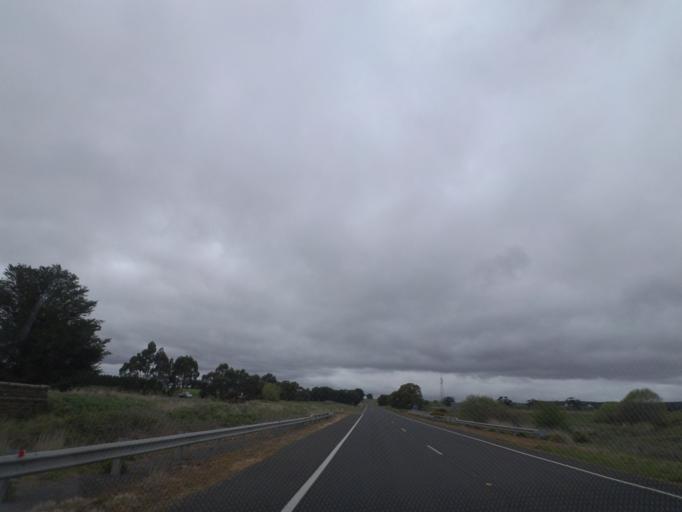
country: AU
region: Victoria
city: Brown Hill
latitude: -37.3764
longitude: 144.0235
